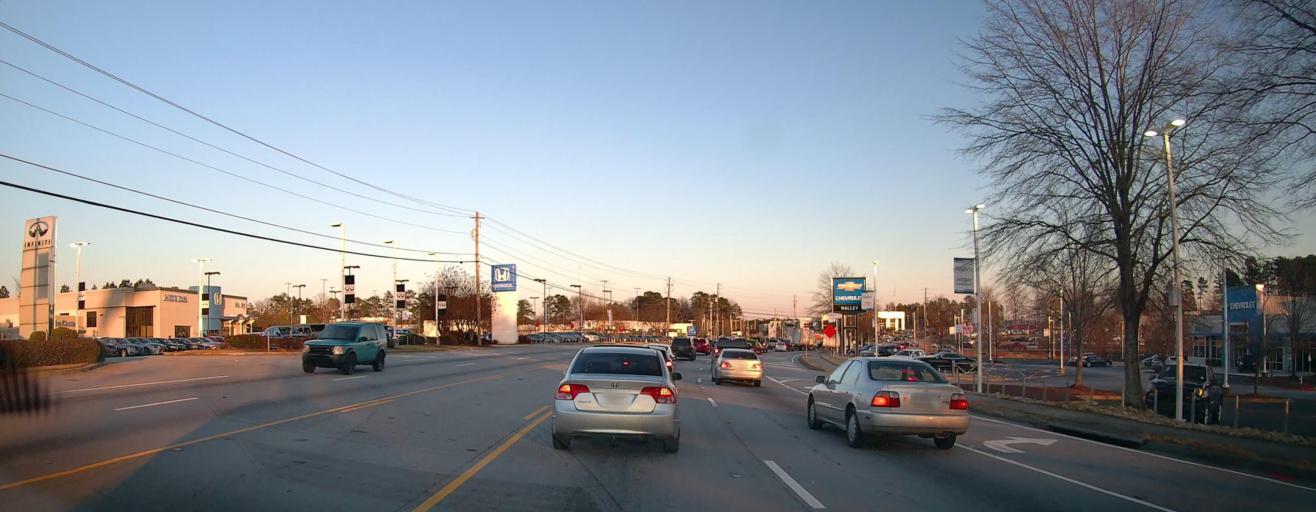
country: US
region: Georgia
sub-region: Fulton County
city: Union City
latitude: 33.5679
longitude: -84.5255
